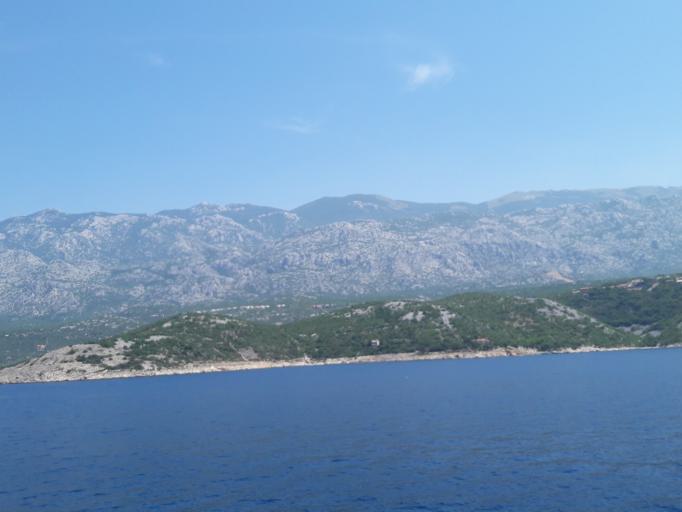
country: HR
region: Primorsko-Goranska
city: Banjol
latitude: 44.7122
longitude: 14.8812
